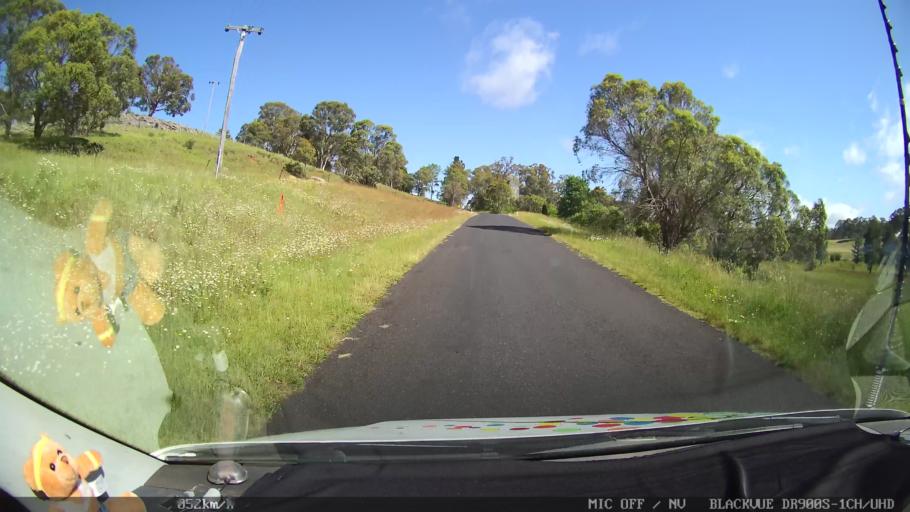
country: AU
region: New South Wales
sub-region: Guyra
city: Guyra
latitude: -30.1114
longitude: 151.6824
